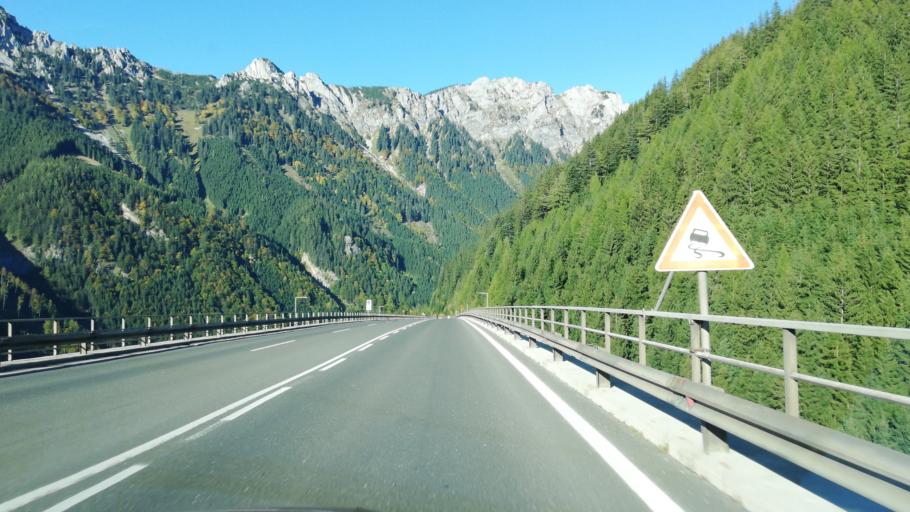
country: AT
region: Styria
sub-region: Politischer Bezirk Leoben
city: Eisenerz
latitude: 47.5394
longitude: 14.9274
